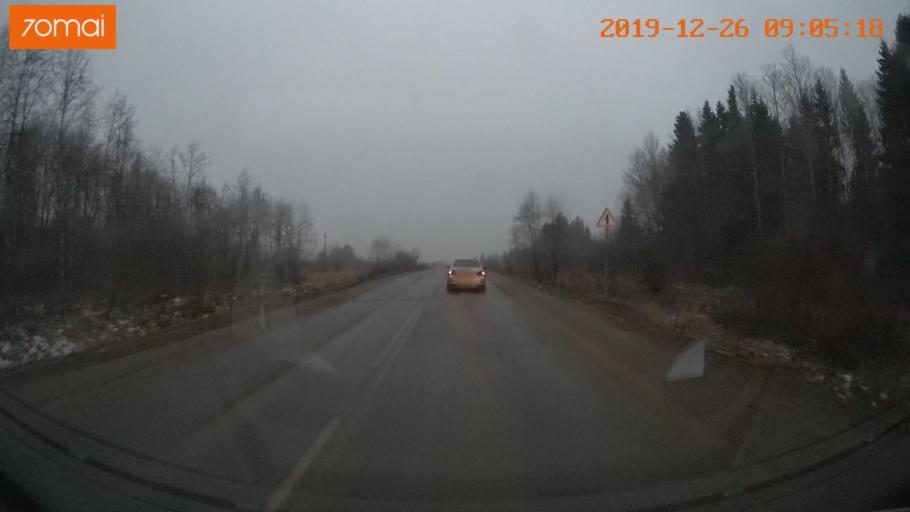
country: RU
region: Vologda
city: Gryazovets
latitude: 58.8242
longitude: 40.2586
